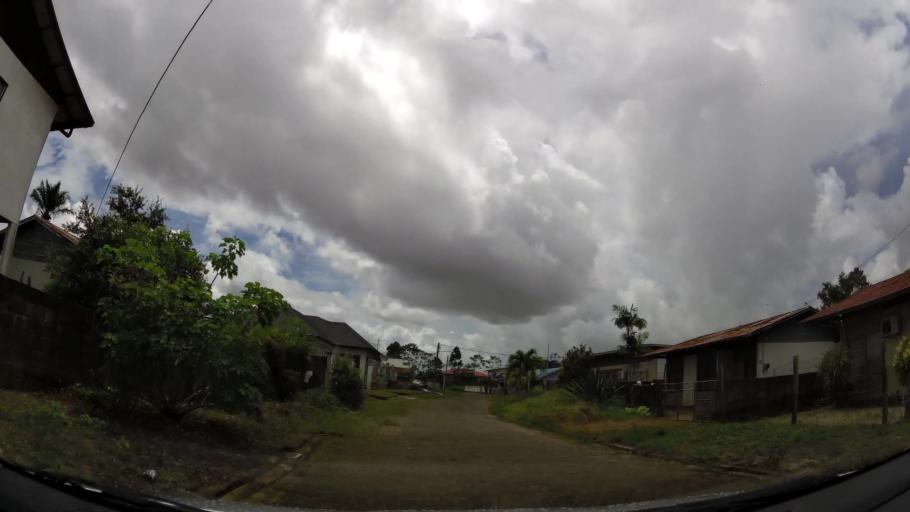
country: SR
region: Paramaribo
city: Paramaribo
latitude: 5.8270
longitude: -55.2233
